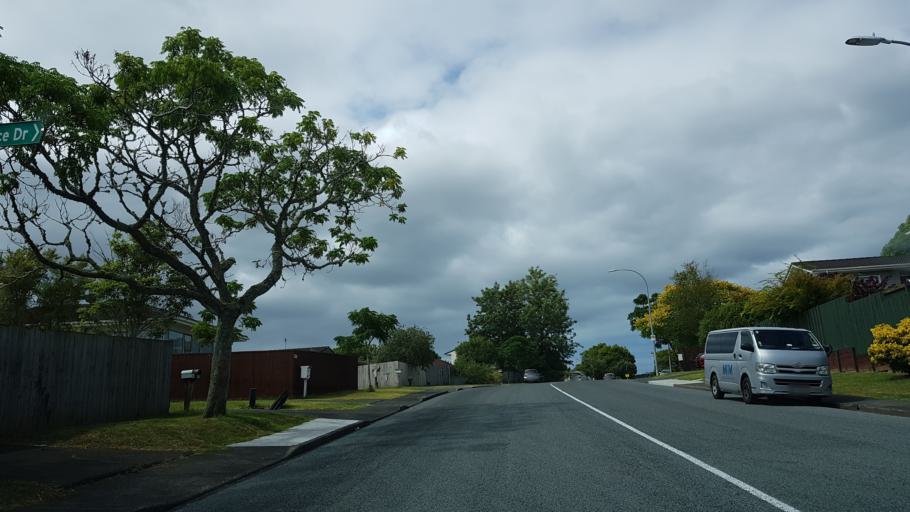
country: NZ
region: Auckland
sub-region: Auckland
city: North Shore
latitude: -36.7727
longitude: 174.7032
